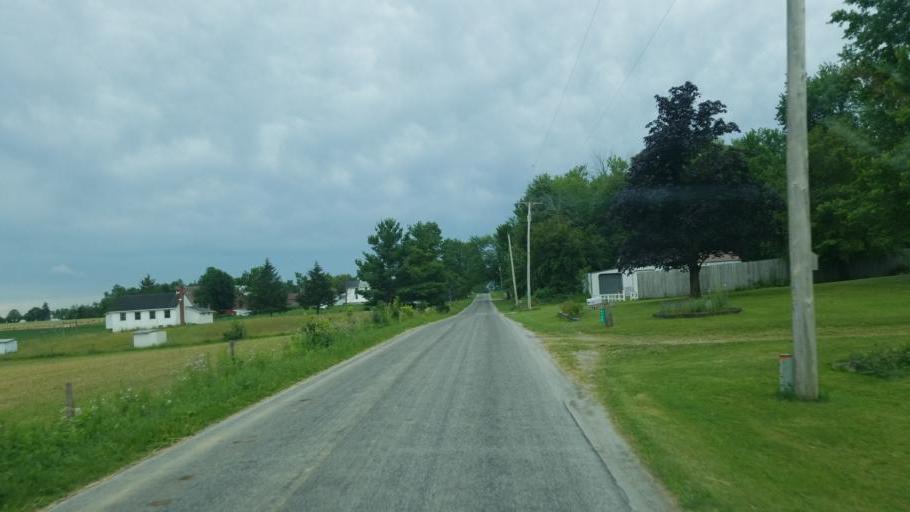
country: US
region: Ohio
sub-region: Huron County
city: Greenwich
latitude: 40.9230
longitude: -82.4747
